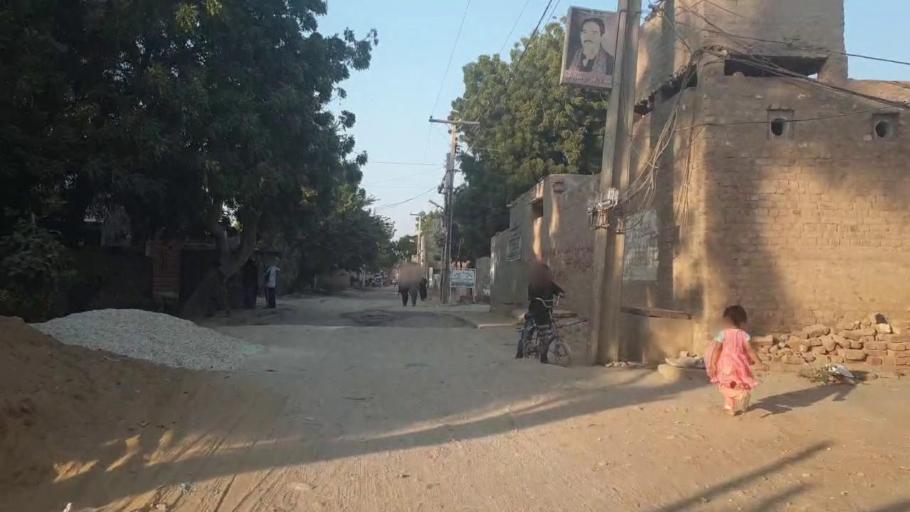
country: PK
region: Sindh
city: Jamshoro
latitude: 25.4421
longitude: 68.2959
